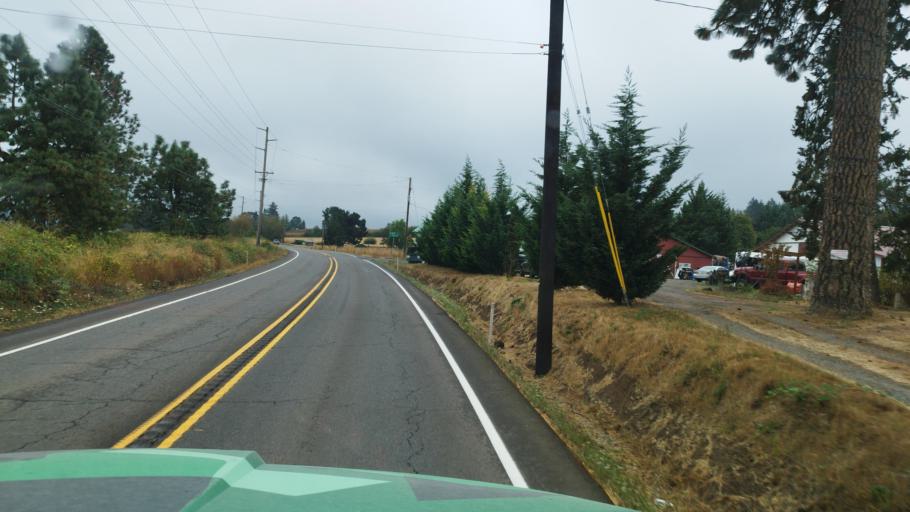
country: US
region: Oregon
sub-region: Yamhill County
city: Yamhill
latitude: 45.4176
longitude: -123.1347
